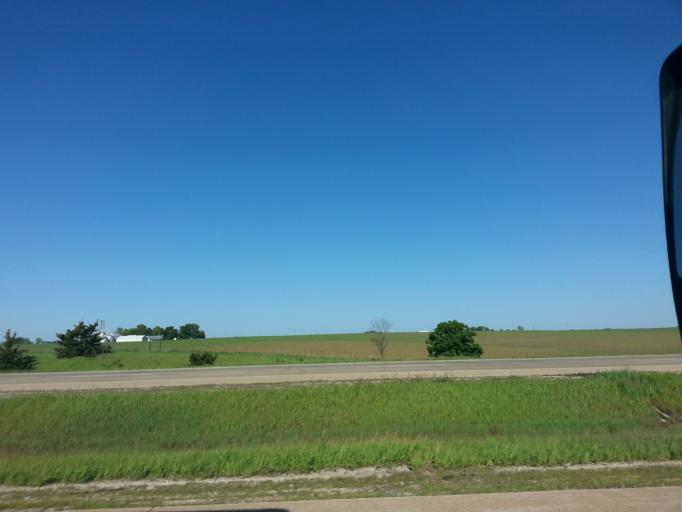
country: US
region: Illinois
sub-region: LaSalle County
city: Oglesby
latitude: 41.1964
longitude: -89.0766
